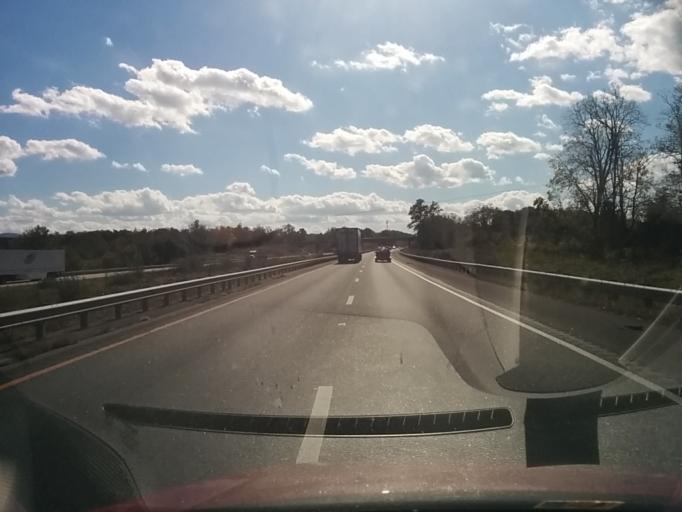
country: US
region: Virginia
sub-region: Augusta County
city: Stuarts Draft
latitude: 37.9825
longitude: -79.1825
